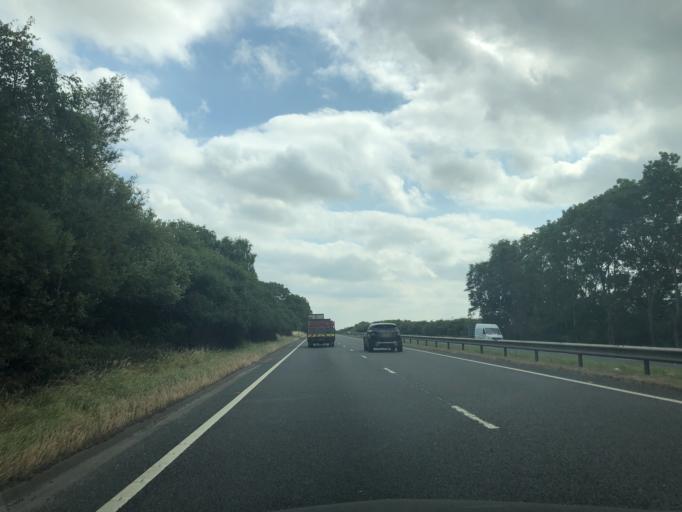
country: GB
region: England
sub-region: Stockton-on-Tees
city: Yarm
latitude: 54.4441
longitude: -1.3230
